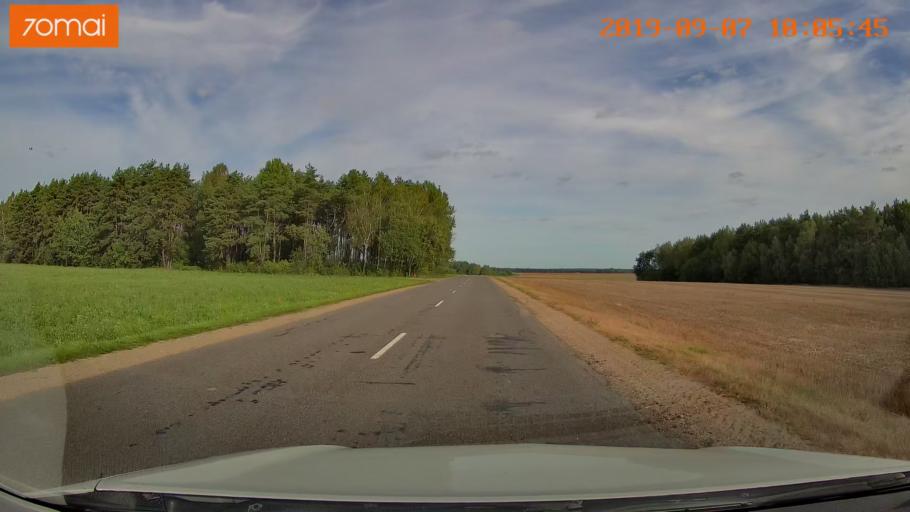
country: BY
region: Grodnenskaya
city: Voranava
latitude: 54.0517
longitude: 25.4059
